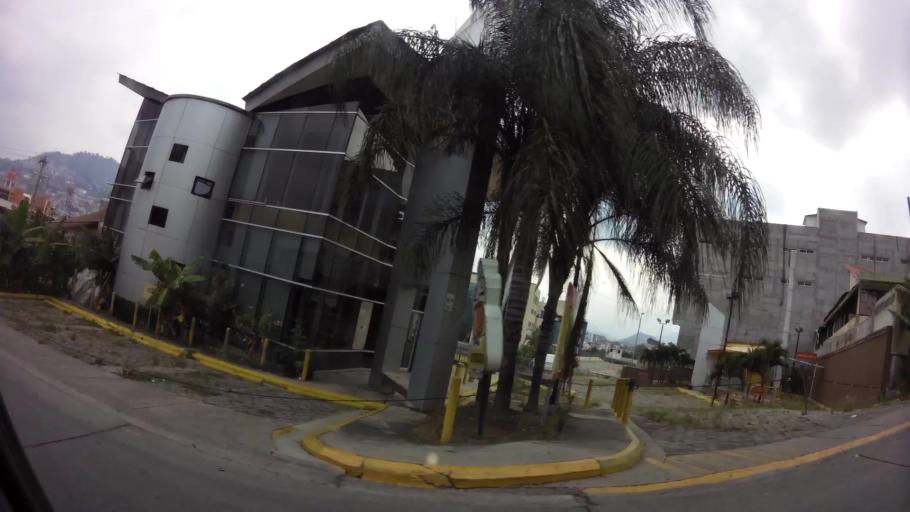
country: HN
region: Francisco Morazan
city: Tegucigalpa
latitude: 14.0946
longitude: -87.1915
